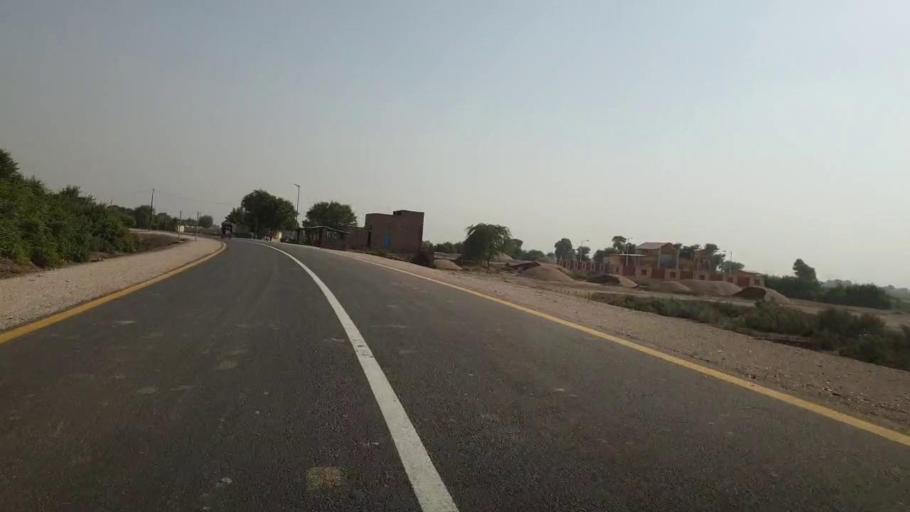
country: PK
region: Sindh
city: Bhan
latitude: 26.5669
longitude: 67.7693
